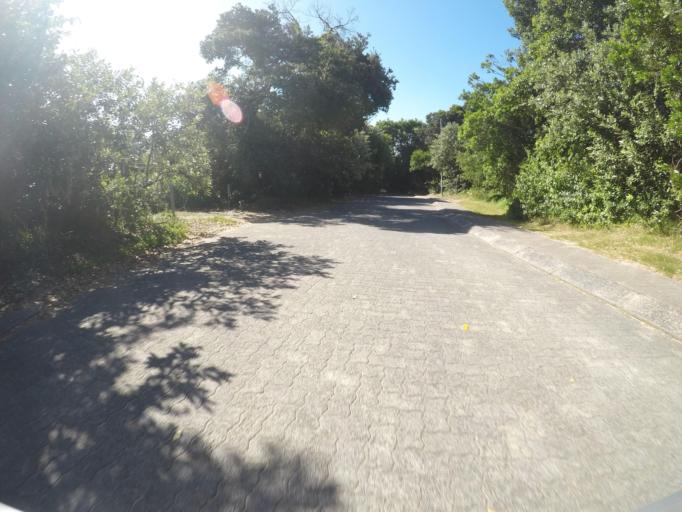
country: ZA
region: Eastern Cape
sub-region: Buffalo City Metropolitan Municipality
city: East London
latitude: -32.9860
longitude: 27.9486
